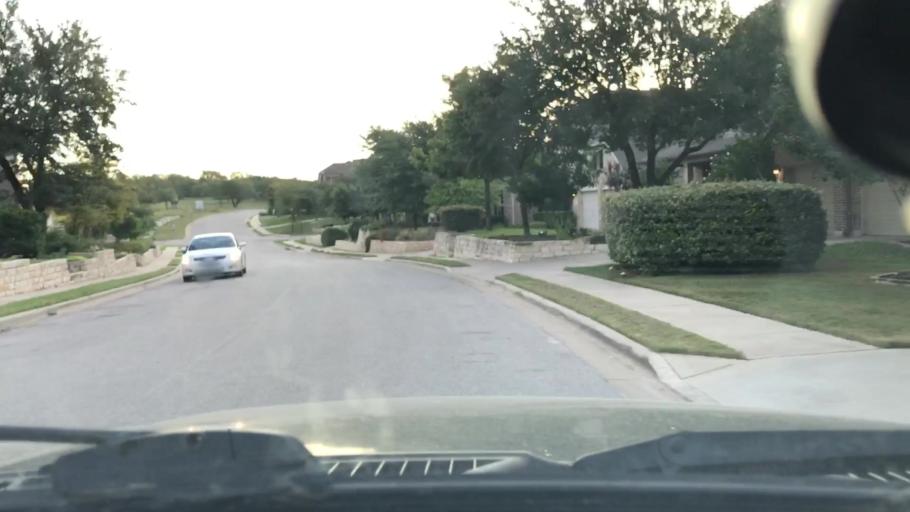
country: US
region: Texas
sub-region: Williamson County
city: Leander
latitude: 30.5408
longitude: -97.8653
